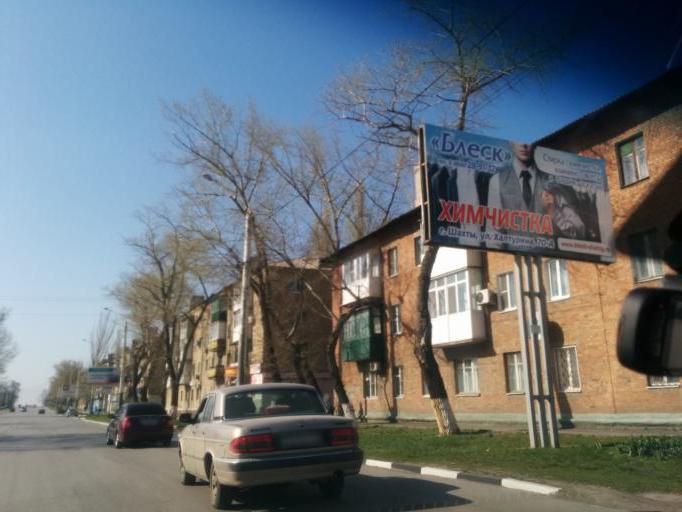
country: RU
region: Rostov
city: Shakhty
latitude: 47.7030
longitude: 40.1982
